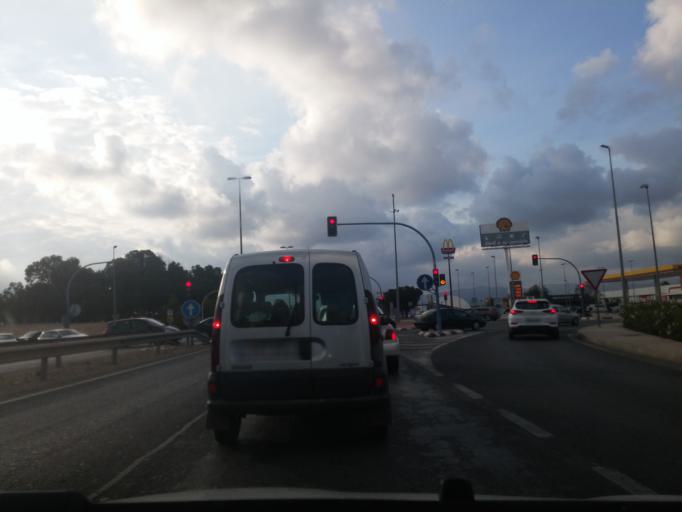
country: ES
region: Valencia
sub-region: Provincia de Alicante
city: San Vicent del Raspeig
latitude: 38.3732
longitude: -0.5067
